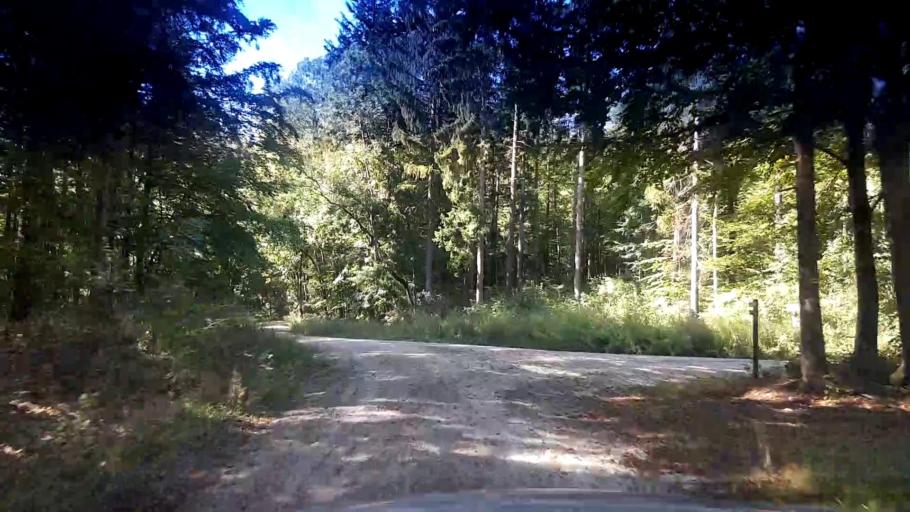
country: DE
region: Bavaria
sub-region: Upper Franconia
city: Poxdorf
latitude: 49.8834
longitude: 11.0766
